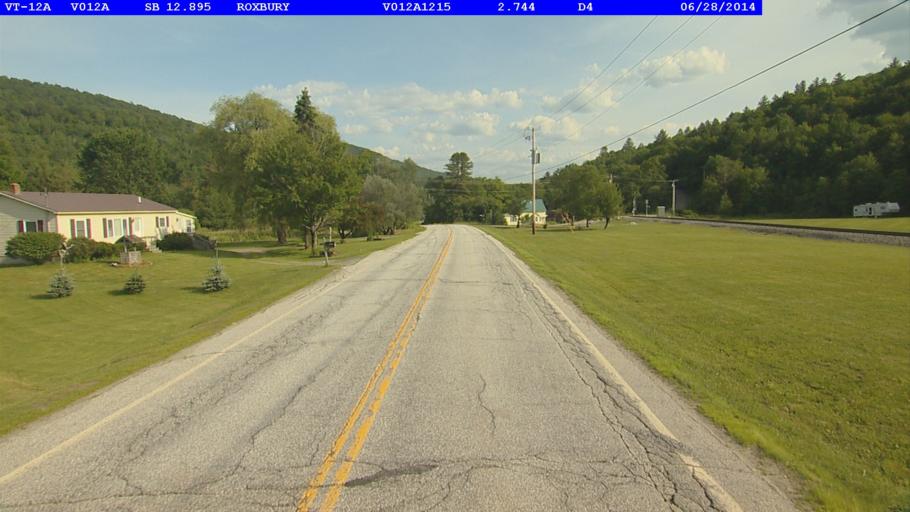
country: US
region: Vermont
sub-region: Washington County
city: Northfield
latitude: 44.0679
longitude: -72.7452
